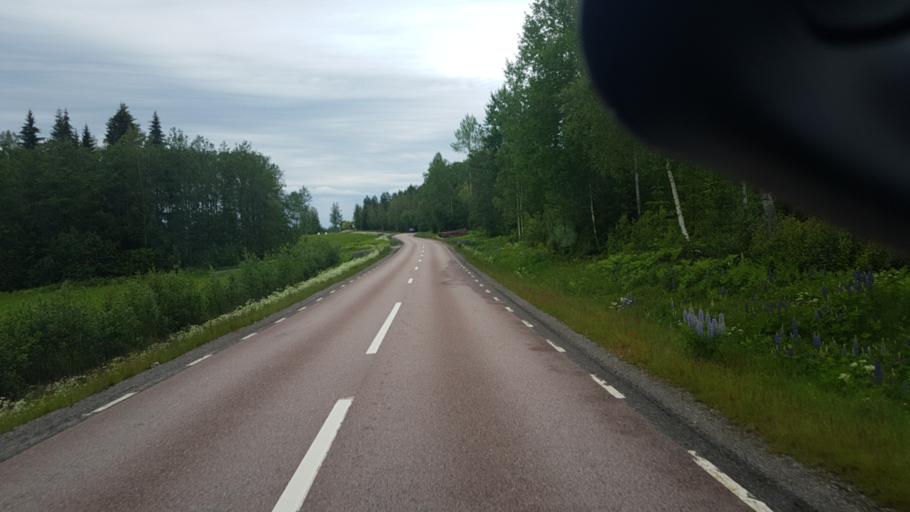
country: SE
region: Vaermland
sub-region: Eda Kommun
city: Amotfors
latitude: 59.7543
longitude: 12.2118
